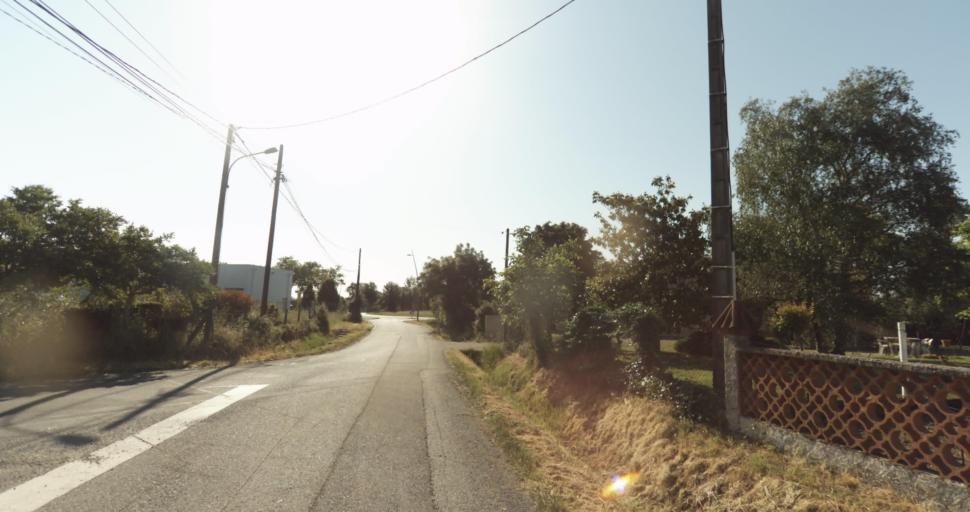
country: FR
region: Midi-Pyrenees
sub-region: Departement de la Haute-Garonne
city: La Salvetat-Saint-Gilles
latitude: 43.5582
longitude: 1.2768
